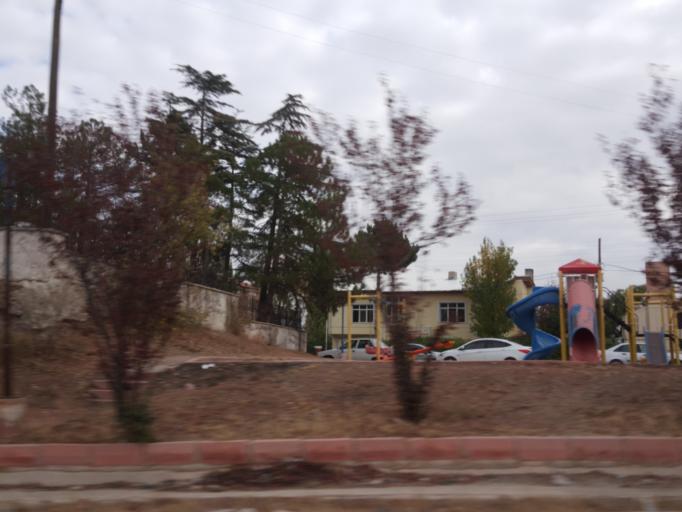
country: TR
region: Kirikkale
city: Keskin
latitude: 39.6708
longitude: 33.6102
